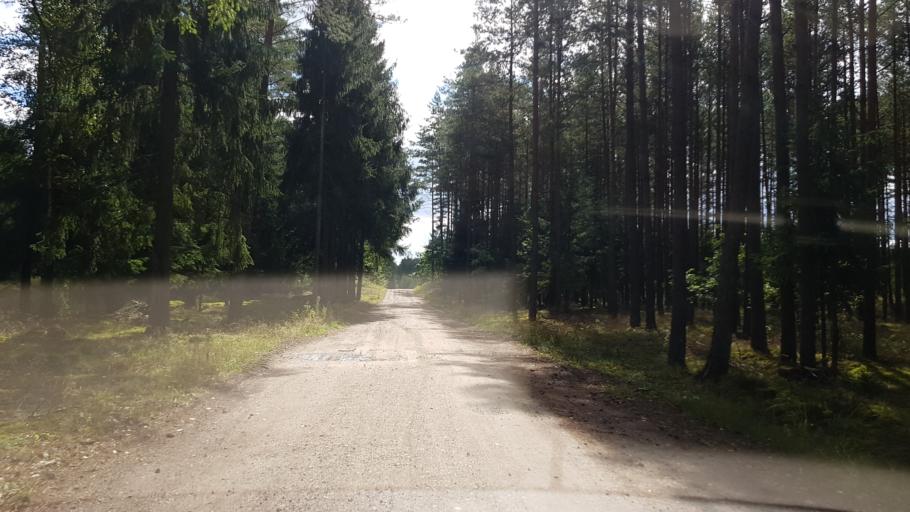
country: PL
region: West Pomeranian Voivodeship
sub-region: Powiat bialogardzki
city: Tychowo
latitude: 54.0119
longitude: 16.3015
